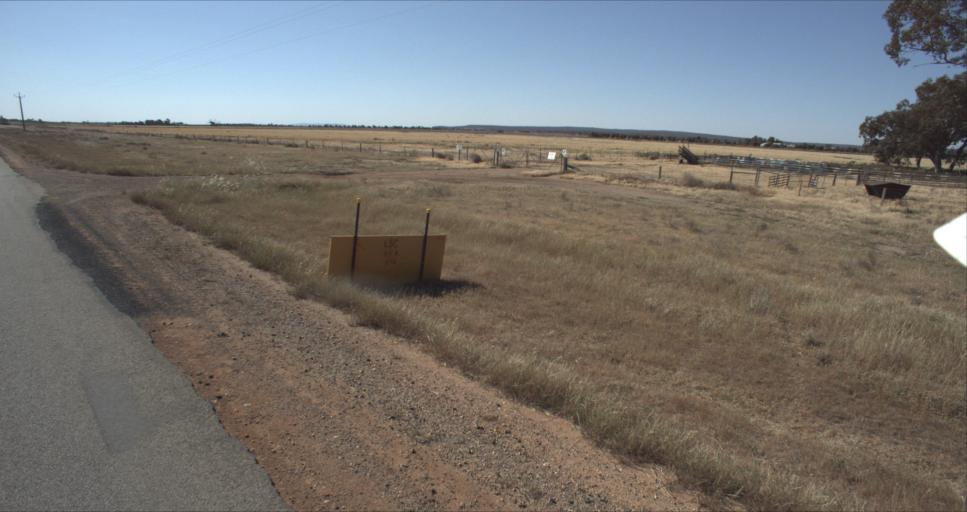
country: AU
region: New South Wales
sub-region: Leeton
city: Leeton
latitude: -34.4966
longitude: 146.3900
